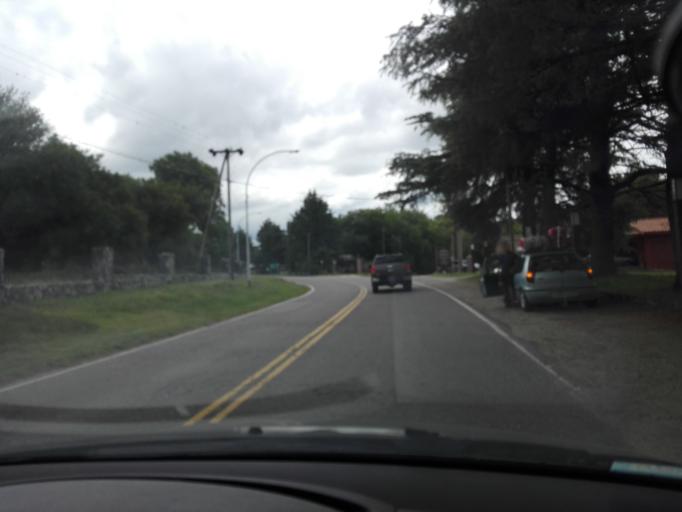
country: AR
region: Cordoba
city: Alta Gracia
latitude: -31.5872
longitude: -64.4598
